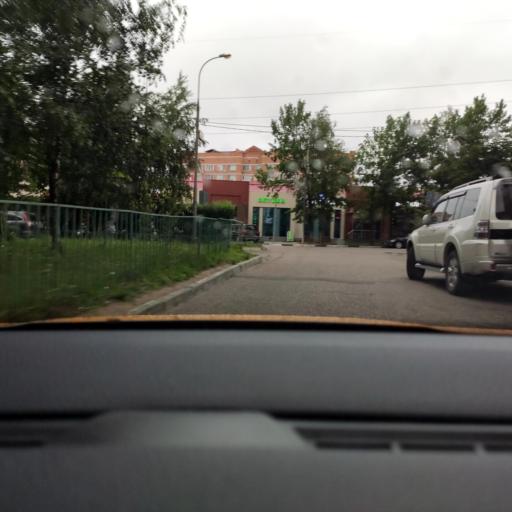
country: RU
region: Moskovskaya
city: Odintsovo
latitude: 55.6888
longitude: 37.2955
